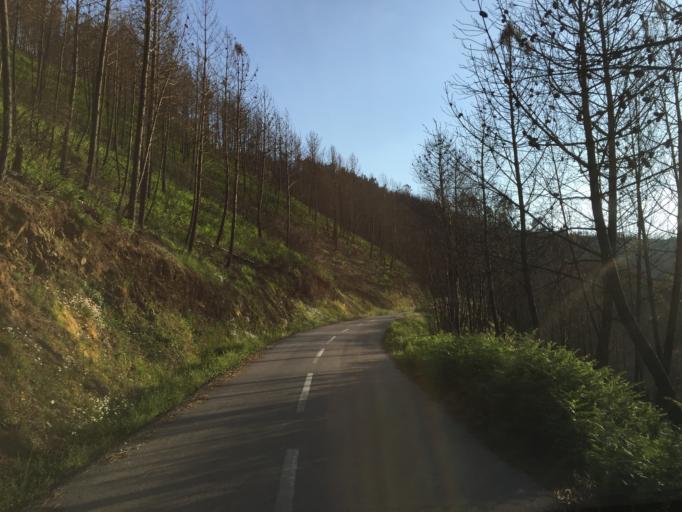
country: PT
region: Coimbra
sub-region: Arganil
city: Arganil
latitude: 40.1373
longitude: -7.9995
